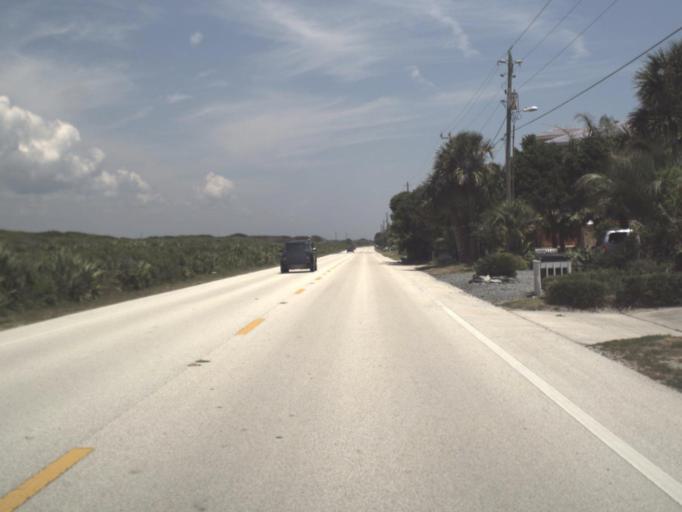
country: US
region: Florida
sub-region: Saint Johns County
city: Villano Beach
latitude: 30.0424
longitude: -81.3283
